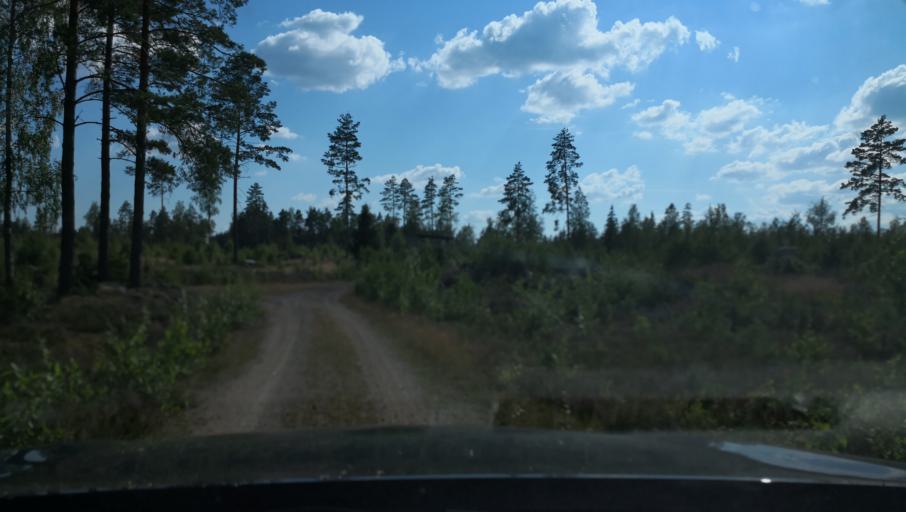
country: SE
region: Vaestmanland
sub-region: Vasteras
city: Skultuna
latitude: 59.7199
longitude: 16.3834
